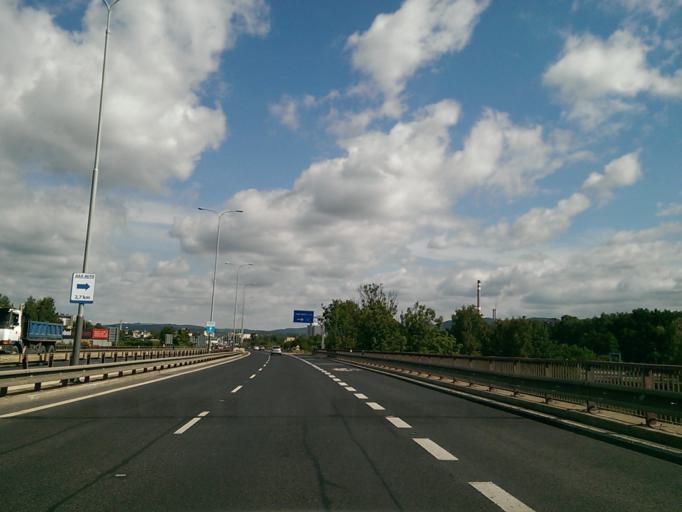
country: CZ
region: Liberecky
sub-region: Okres Liberec
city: Liberec
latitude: 50.7485
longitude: 15.0543
